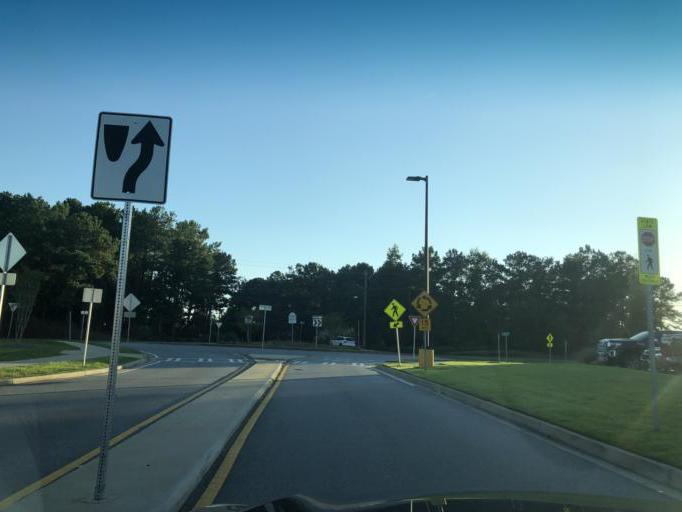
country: US
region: Georgia
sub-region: Muscogee County
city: Columbus
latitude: 32.5523
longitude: -84.8972
